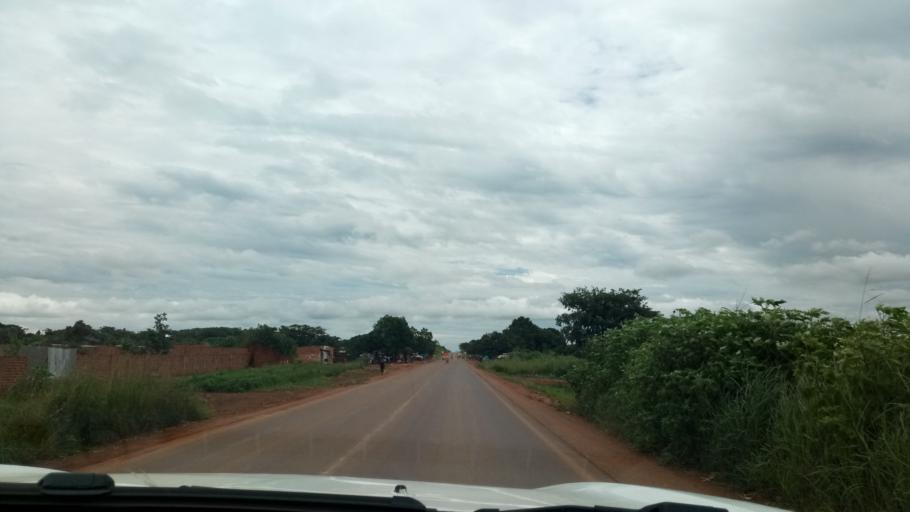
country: CD
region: Katanga
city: Lubumbashi
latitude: -11.5538
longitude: 27.5850
